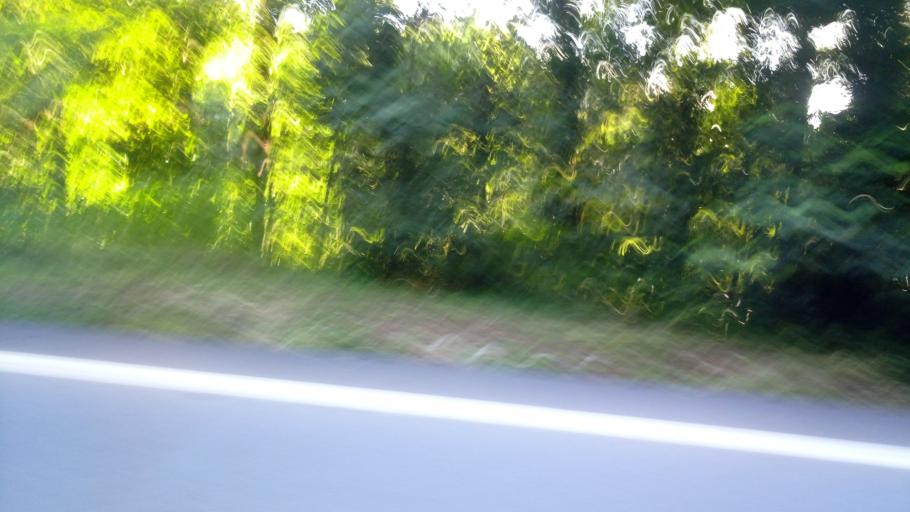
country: AU
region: Queensland
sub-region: Cassowary Coast
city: Innisfail
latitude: -17.6057
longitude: 145.7686
